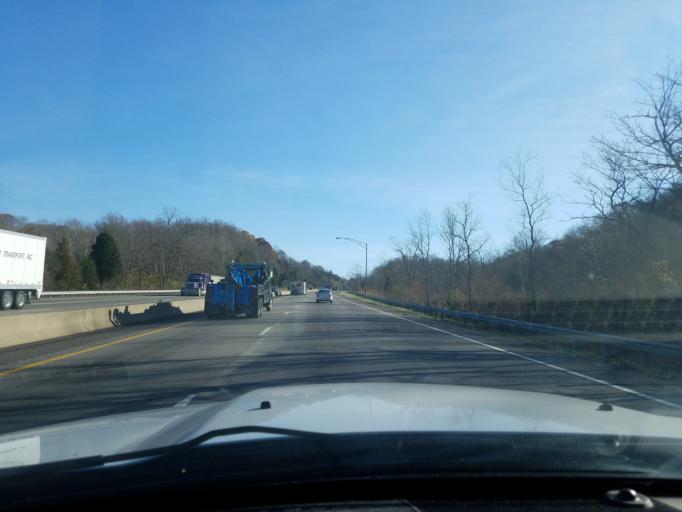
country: US
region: Ohio
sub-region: Clermont County
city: Batavia
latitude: 39.0862
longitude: -84.1717
